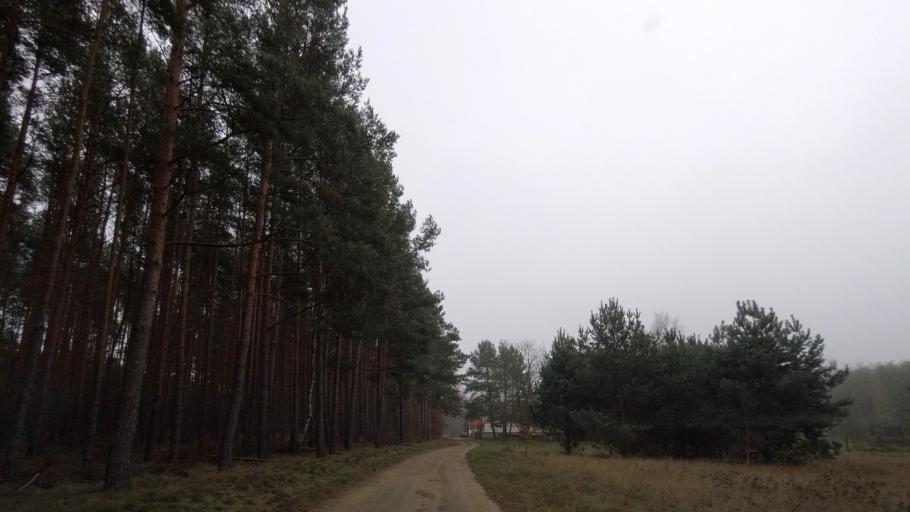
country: DE
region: Brandenburg
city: Treuenbrietzen
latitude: 52.0560
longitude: 12.8908
